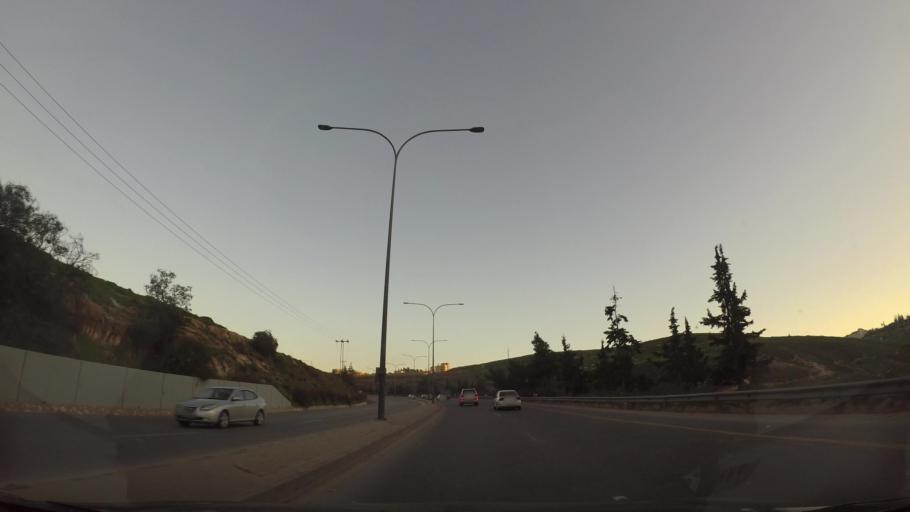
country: JO
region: Amman
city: Umm as Summaq
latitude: 31.8638
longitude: 35.7918
